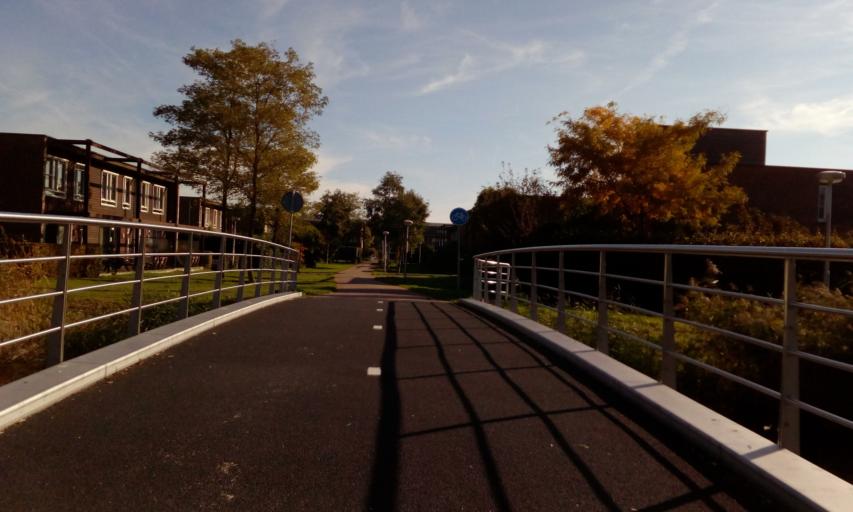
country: NL
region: Utrecht
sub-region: Stichtse Vecht
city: Maarssen
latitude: 52.1057
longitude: 5.0350
